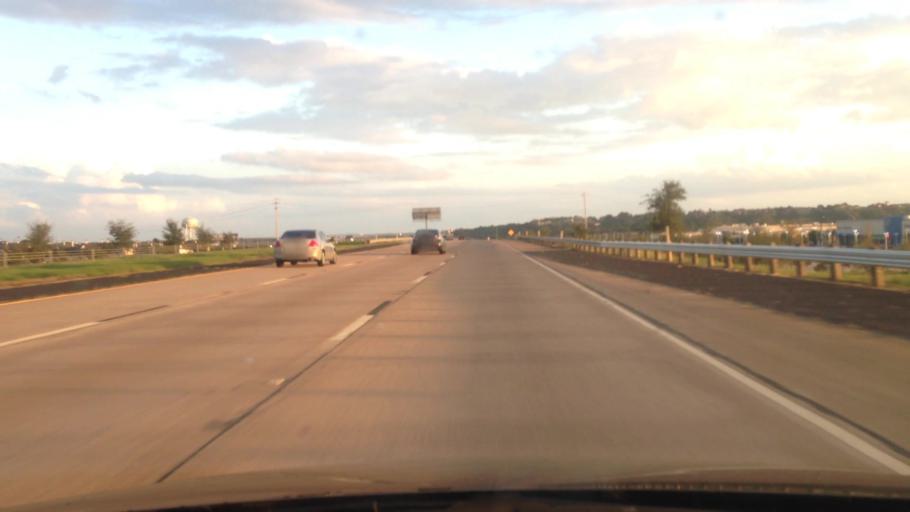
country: US
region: Texas
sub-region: Tarrant County
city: White Settlement
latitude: 32.7265
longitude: -97.4809
